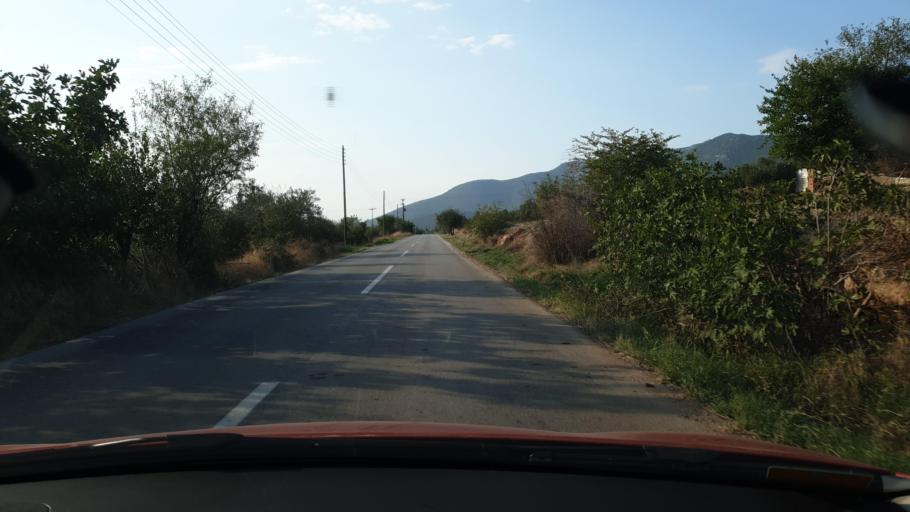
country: GR
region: Thessaly
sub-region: Nomos Magnisias
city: Sourpi
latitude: 39.0918
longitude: 22.9037
